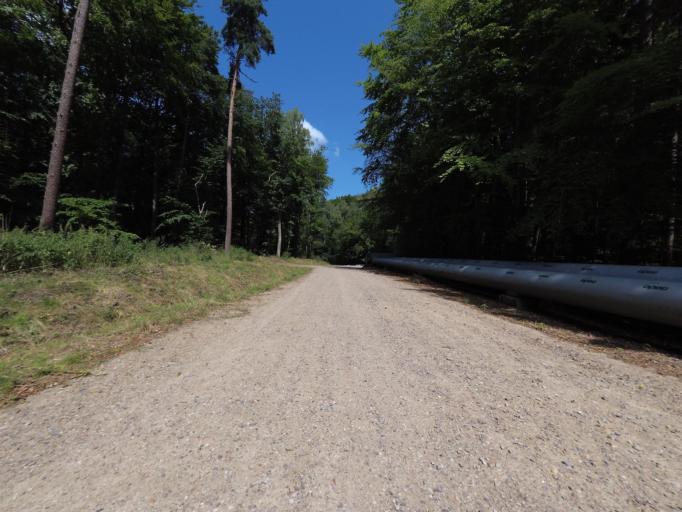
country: PL
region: Pomeranian Voivodeship
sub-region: Gdynia
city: Wielki Kack
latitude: 54.4871
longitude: 18.5022
